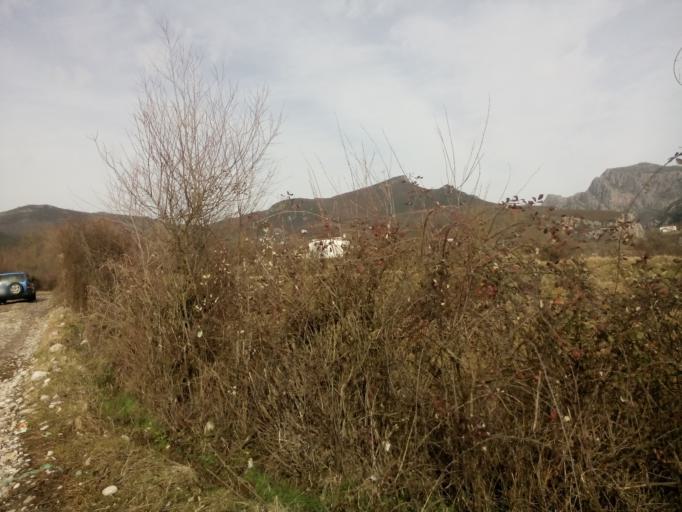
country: AL
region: Diber
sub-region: Rrethi i Matit
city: Rukaj
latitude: 41.6930
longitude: 20.0056
